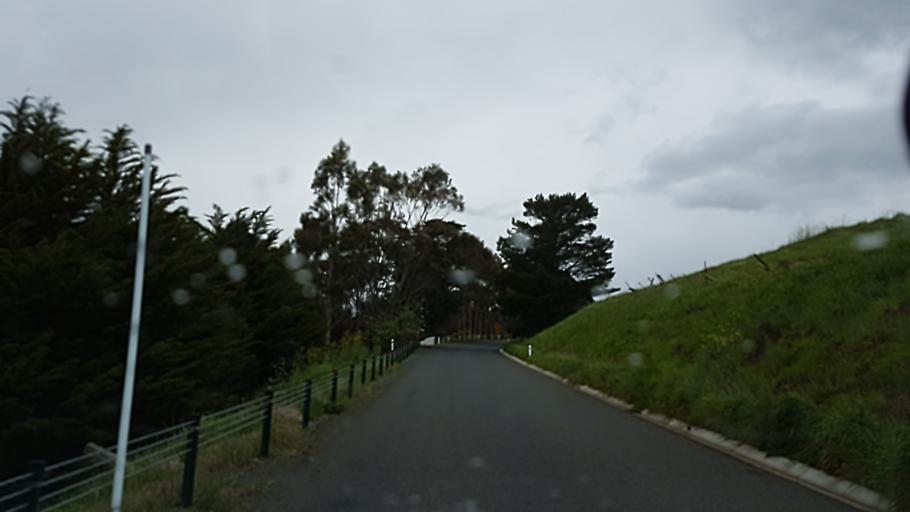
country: AU
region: Victoria
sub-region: Ballarat North
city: Mount Clear
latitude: -37.7782
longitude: 144.1112
